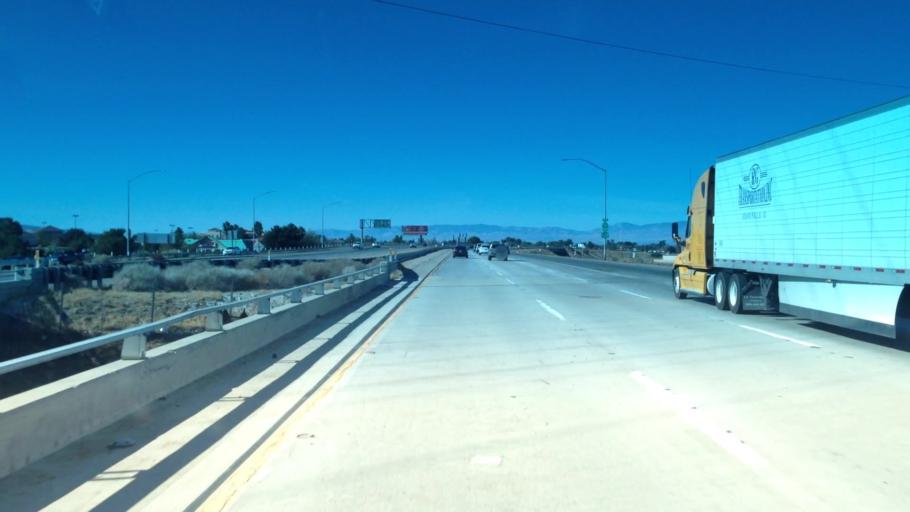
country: US
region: California
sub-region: Los Angeles County
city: Desert View Highlands
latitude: 34.6063
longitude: -118.1460
